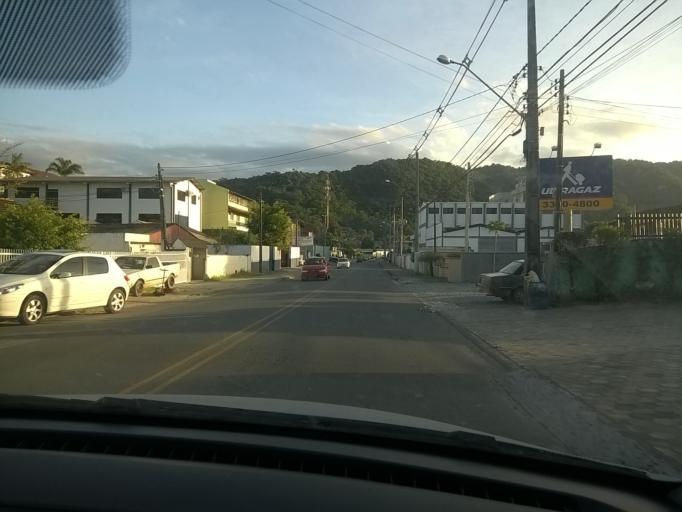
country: BR
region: Santa Catarina
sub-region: Blumenau
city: Blumenau
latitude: -26.9301
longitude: -49.1351
